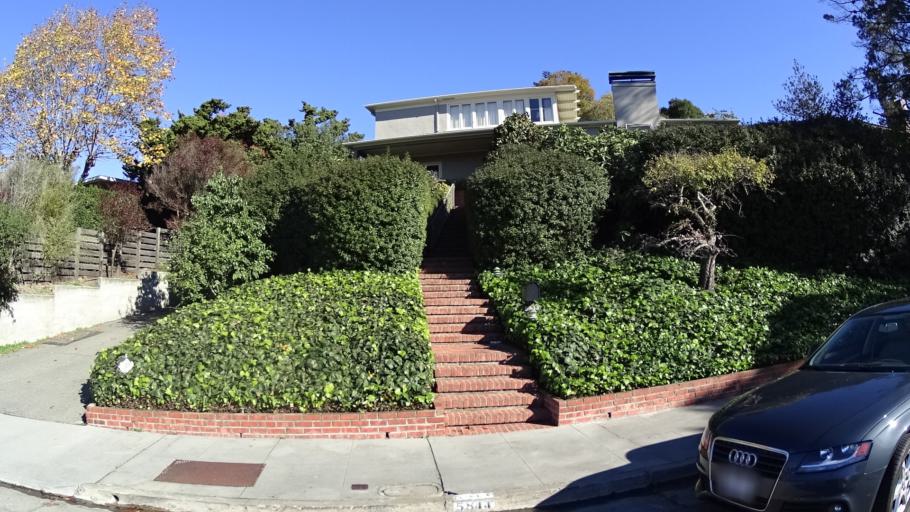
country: US
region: California
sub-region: Alameda County
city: Piedmont
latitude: 37.8440
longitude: -122.2430
